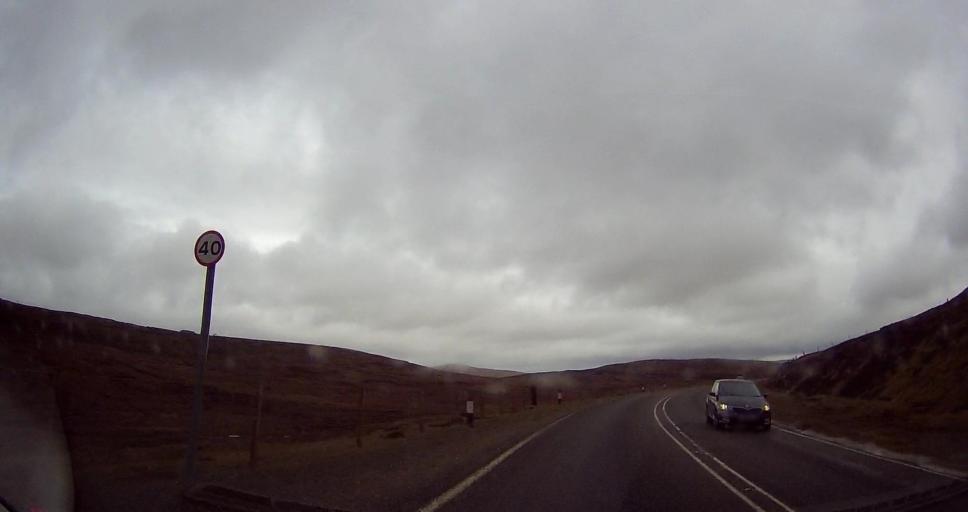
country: GB
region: Scotland
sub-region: Shetland Islands
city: Lerwick
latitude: 60.3217
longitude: -1.2510
